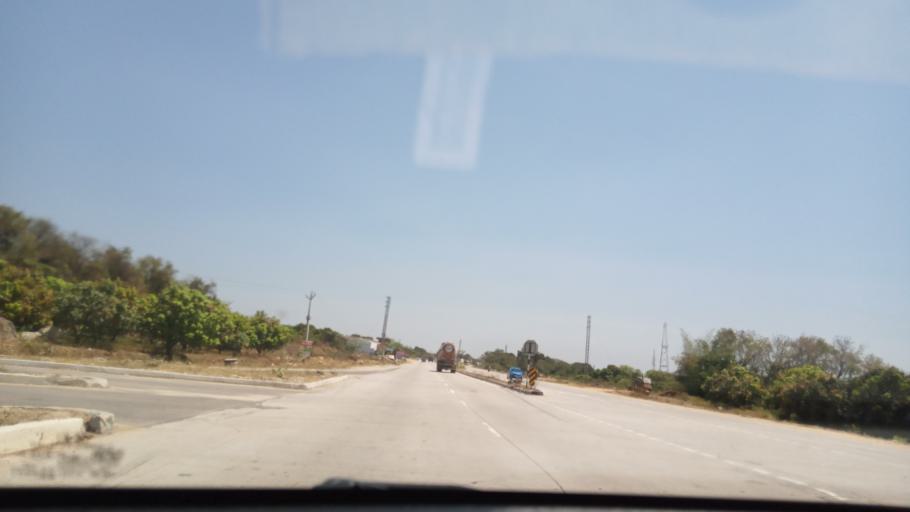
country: IN
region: Andhra Pradesh
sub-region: Chittoor
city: Chittoor
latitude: 13.1967
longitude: 78.9931
